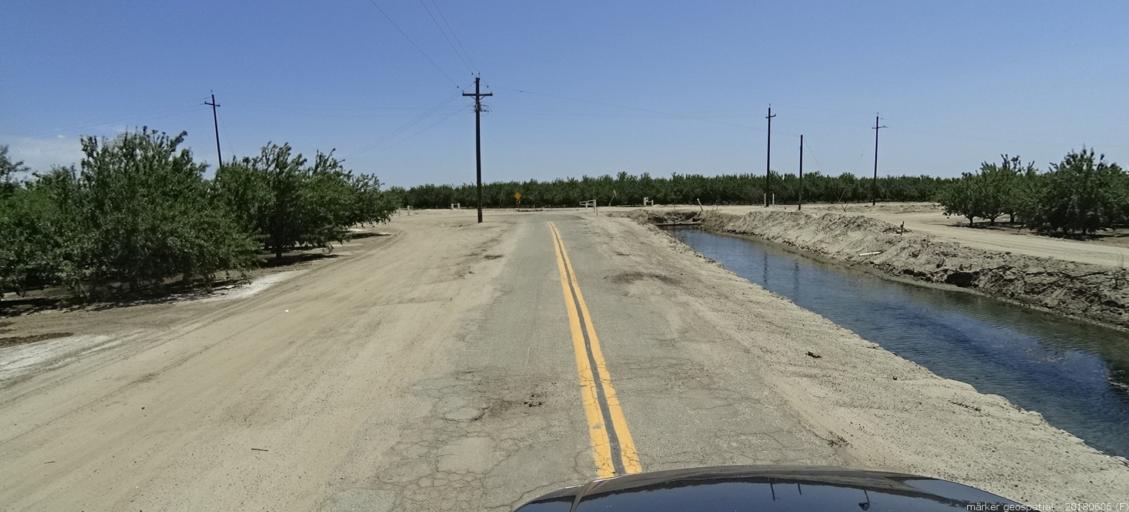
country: US
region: California
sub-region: Fresno County
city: Mendota
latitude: 36.7872
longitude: -120.3108
